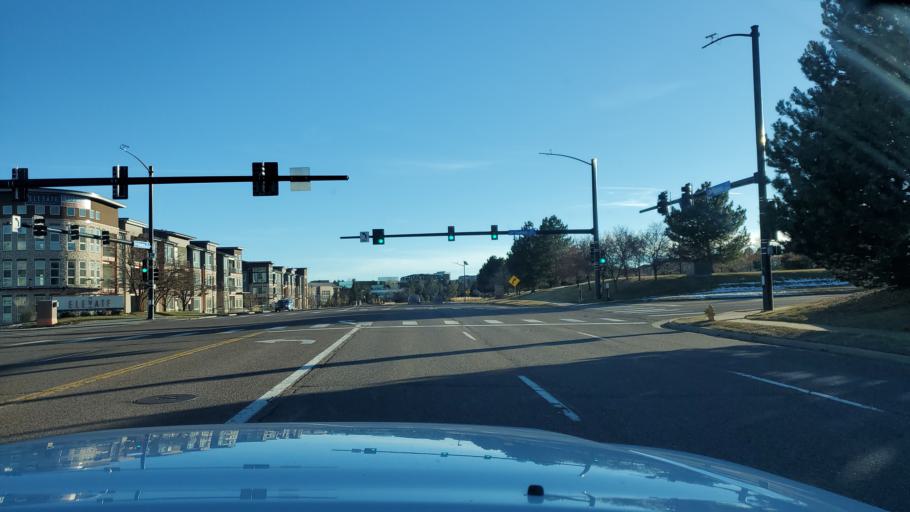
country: US
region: Colorado
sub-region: Arapahoe County
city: Centennial
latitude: 39.5846
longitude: -104.8669
